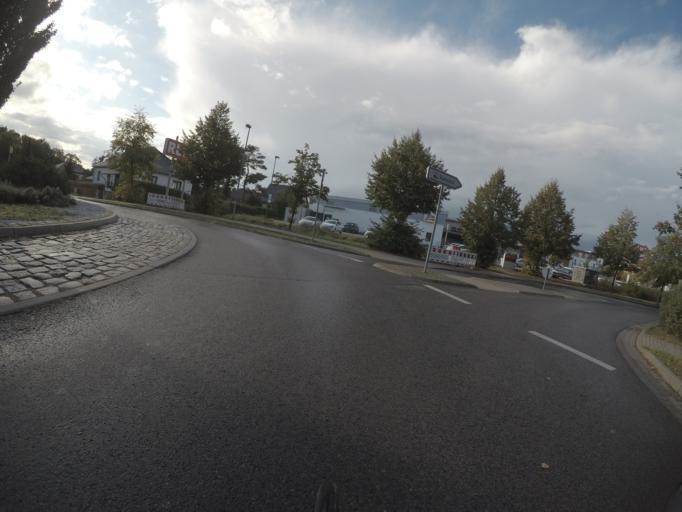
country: DE
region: Brandenburg
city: Petershagen
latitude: 52.5238
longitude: 13.7634
